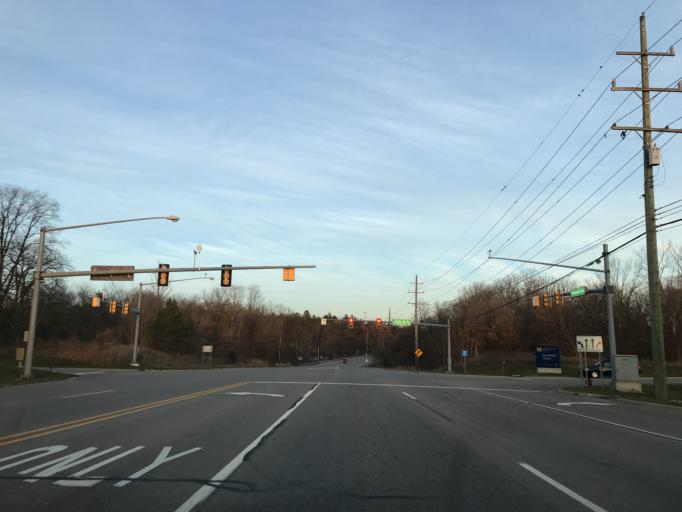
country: US
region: Michigan
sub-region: Washtenaw County
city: Ann Arbor
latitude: 42.3106
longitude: -83.6732
